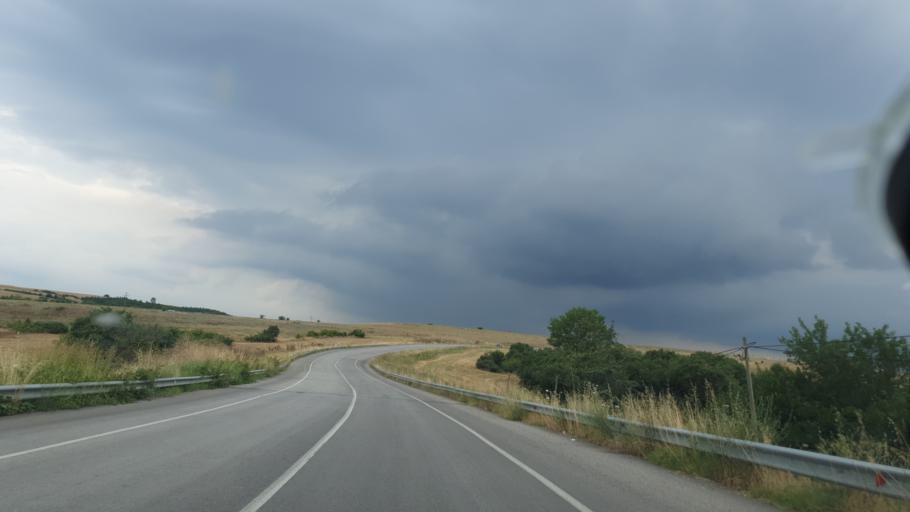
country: TR
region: Tekirdag
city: Hayrabolu
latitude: 41.2197
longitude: 27.0638
